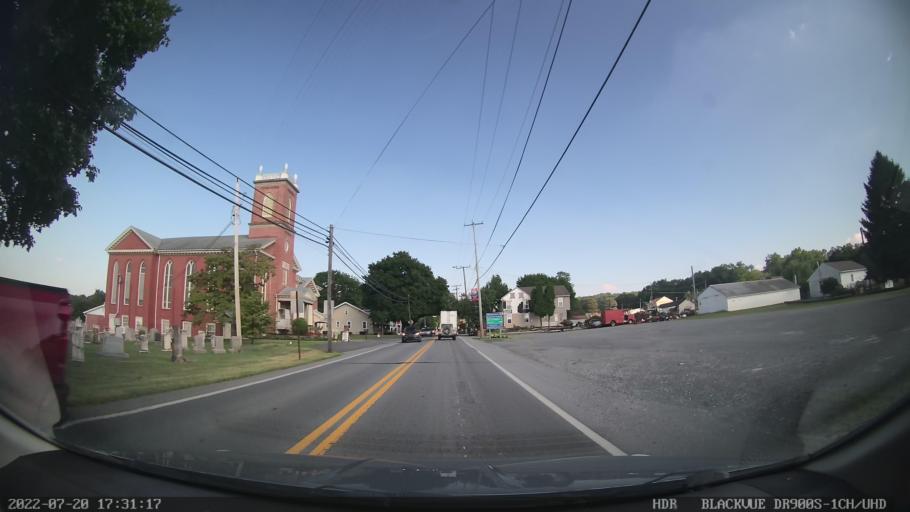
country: US
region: Pennsylvania
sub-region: Berks County
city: Blandon
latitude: 40.4420
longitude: -75.8880
